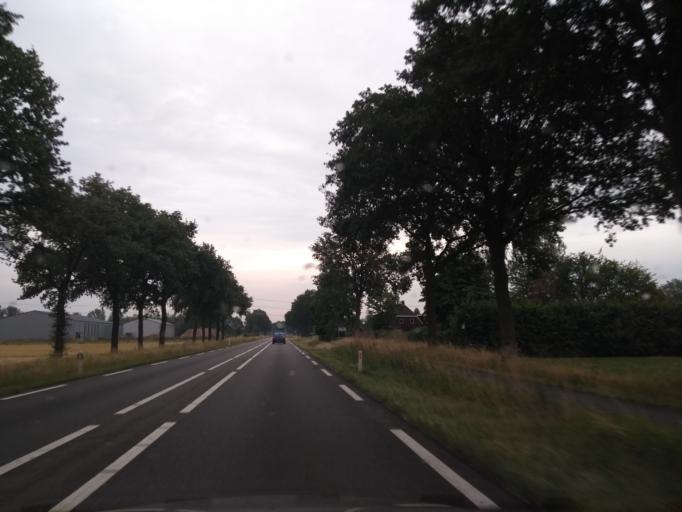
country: NL
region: Gelderland
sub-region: Oude IJsselstreek
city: Gendringen
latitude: 51.9091
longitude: 6.3228
